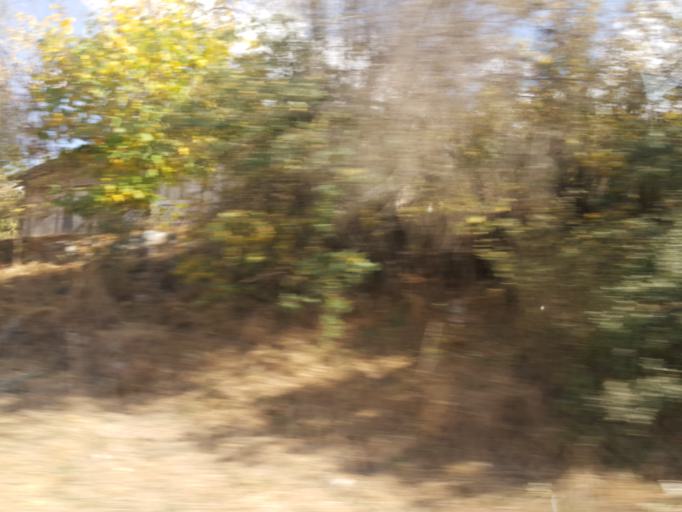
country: TR
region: Tokat
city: Artova
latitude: 40.0426
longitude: 36.2992
